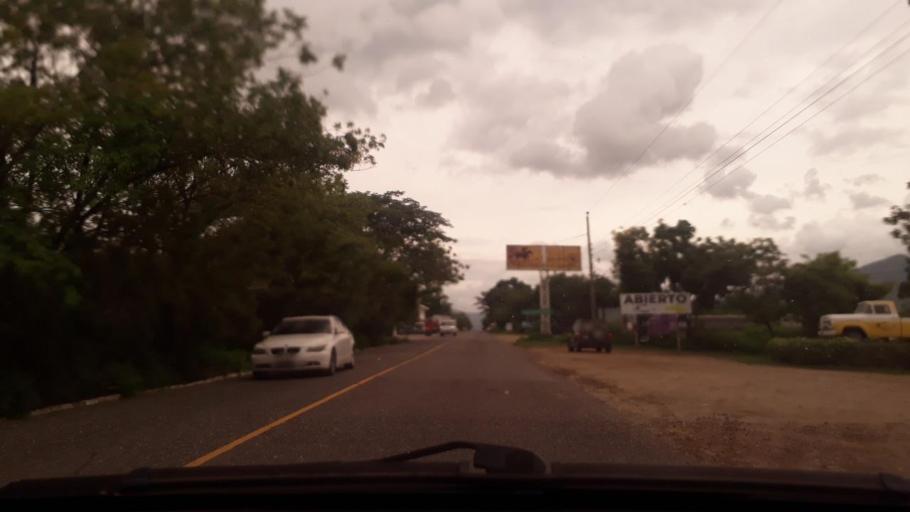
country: GT
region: Chiquimula
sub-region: Municipio de Chiquimula
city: Chiquimula
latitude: 14.7486
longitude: -89.5375
